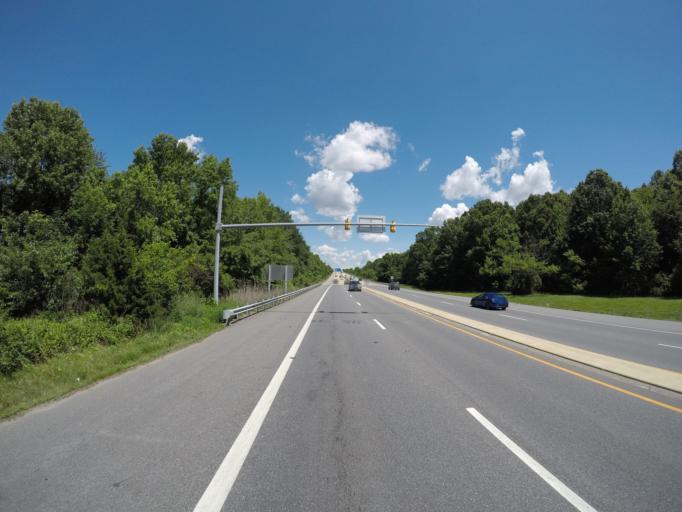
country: US
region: Delaware
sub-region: New Castle County
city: Glasgow
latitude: 39.5316
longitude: -75.7375
